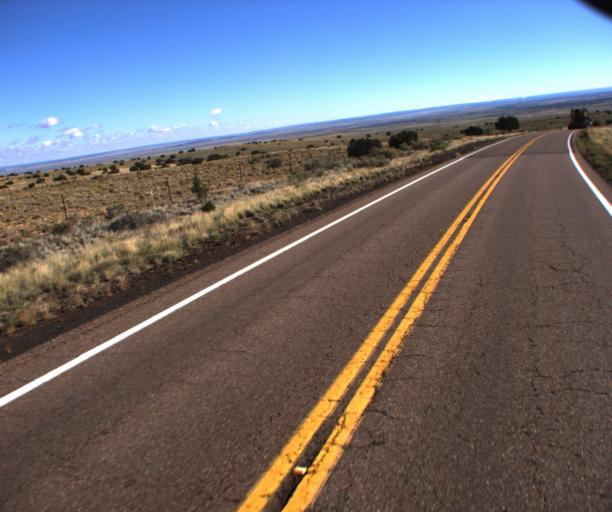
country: US
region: Arizona
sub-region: Apache County
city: Saint Johns
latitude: 34.4992
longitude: -109.5023
